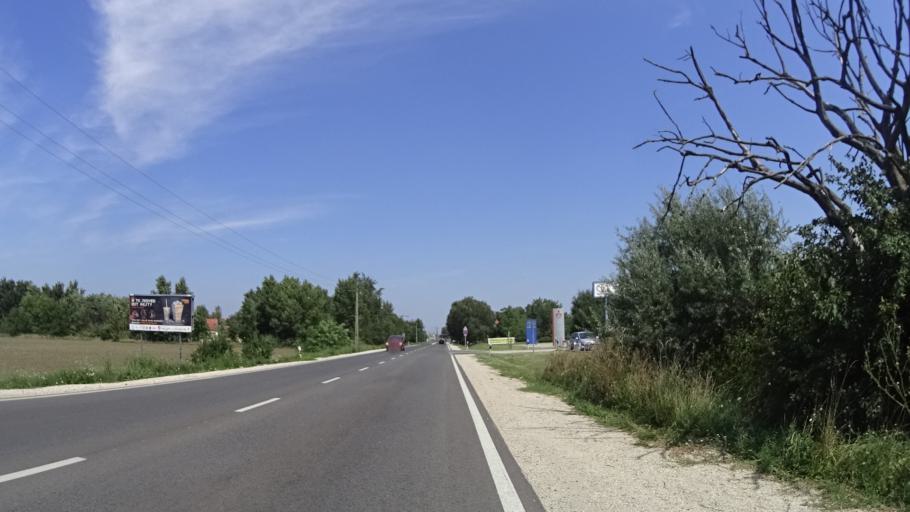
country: HU
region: Fejer
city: Szekesfehervar
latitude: 47.1557
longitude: 18.3995
